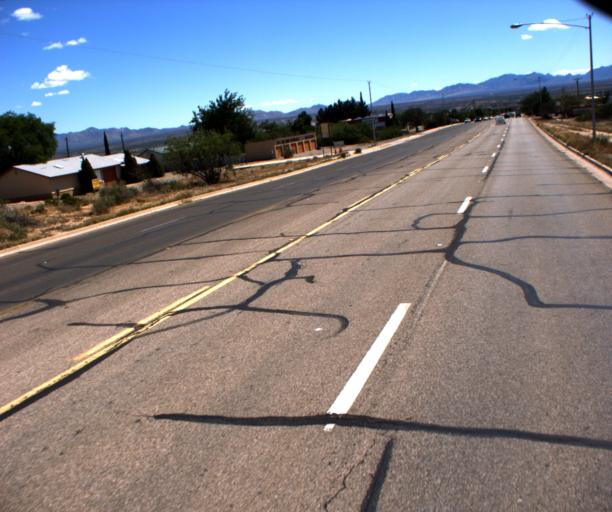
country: US
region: Arizona
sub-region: Cochise County
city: Benson
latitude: 31.9713
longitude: -110.3198
